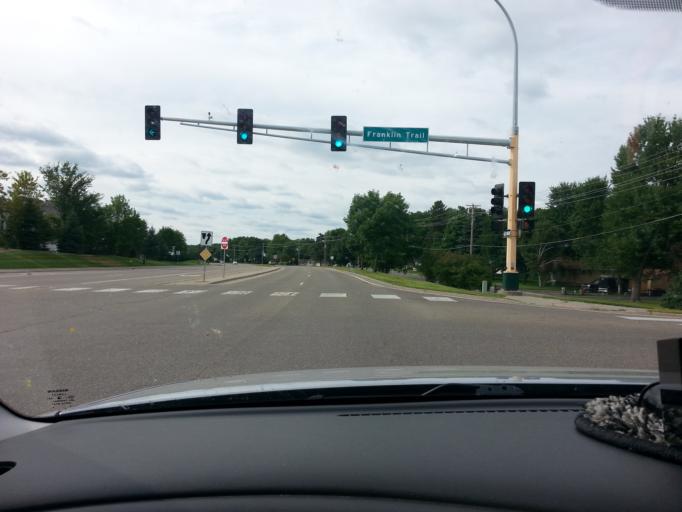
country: US
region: Minnesota
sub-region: Scott County
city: Prior Lake
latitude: 44.7107
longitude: -93.4162
